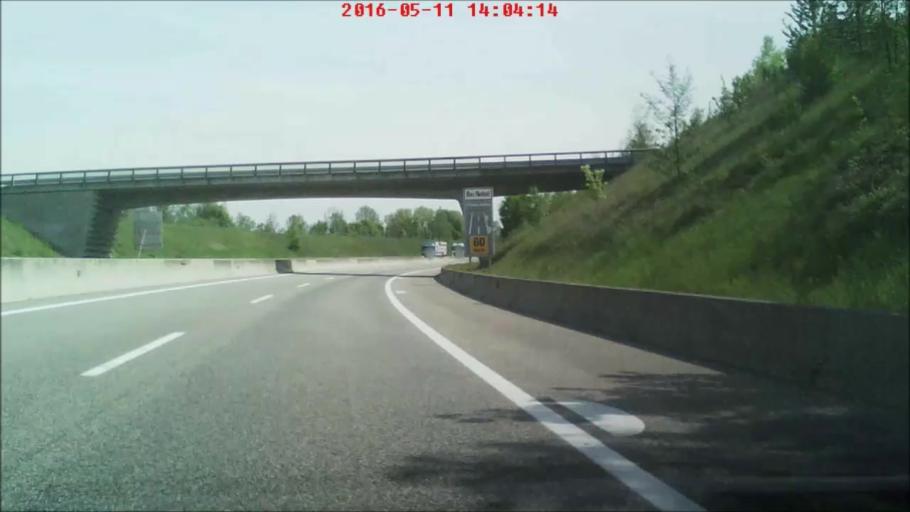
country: AT
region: Upper Austria
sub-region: Wels-Land
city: Steinhaus
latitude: 48.1357
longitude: 14.0016
